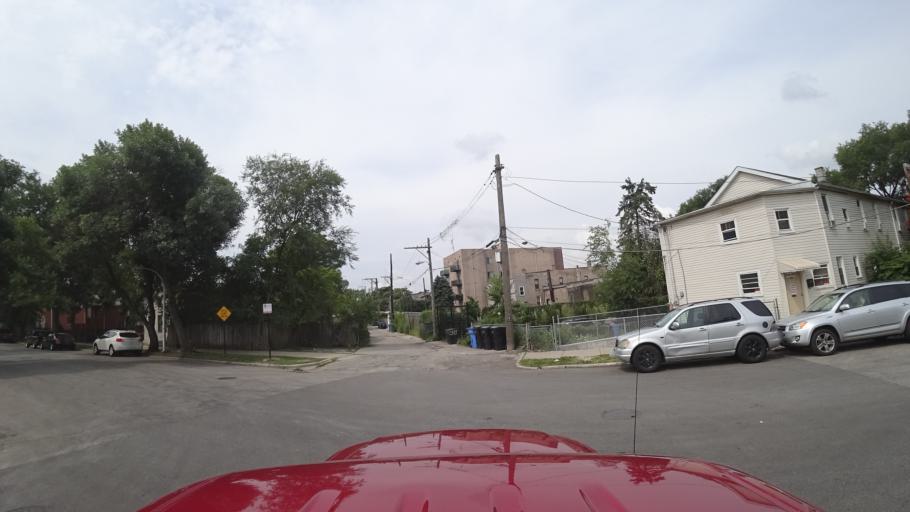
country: US
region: Illinois
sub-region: Cook County
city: Chicago
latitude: 41.8356
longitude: -87.6680
